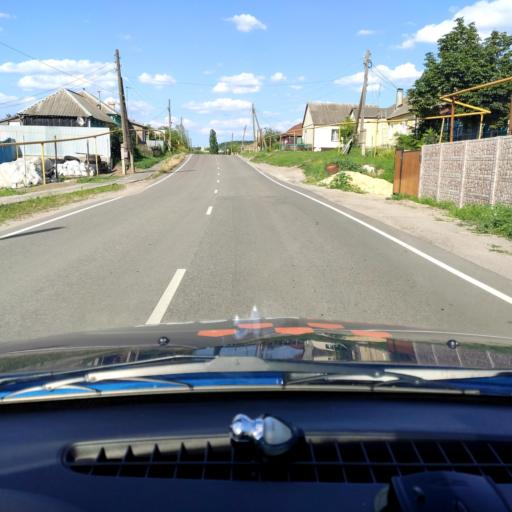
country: RU
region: Voronezj
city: Devitsa
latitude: 51.6431
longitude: 38.9575
